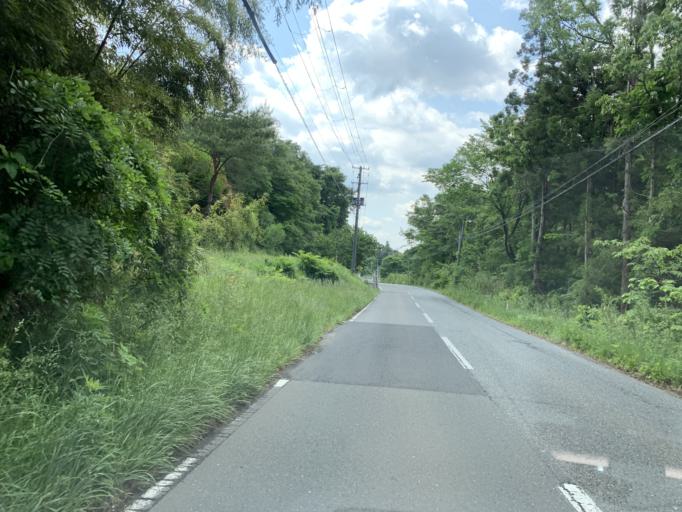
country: JP
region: Miyagi
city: Furukawa
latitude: 38.7746
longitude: 140.9609
